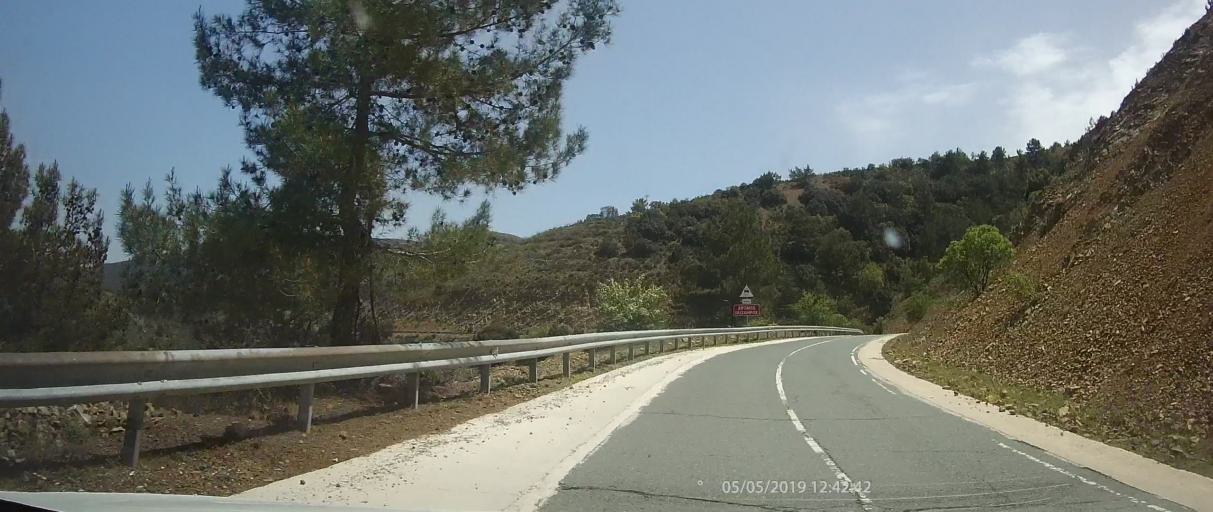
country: CY
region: Lefkosia
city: Kakopetria
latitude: 34.9721
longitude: 32.8118
